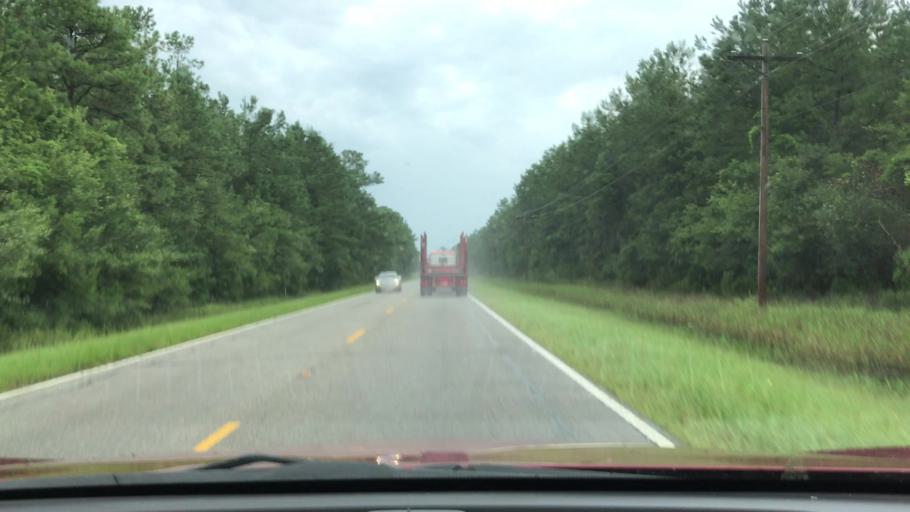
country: US
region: South Carolina
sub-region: Georgetown County
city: Georgetown
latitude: 33.5035
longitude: -79.2566
